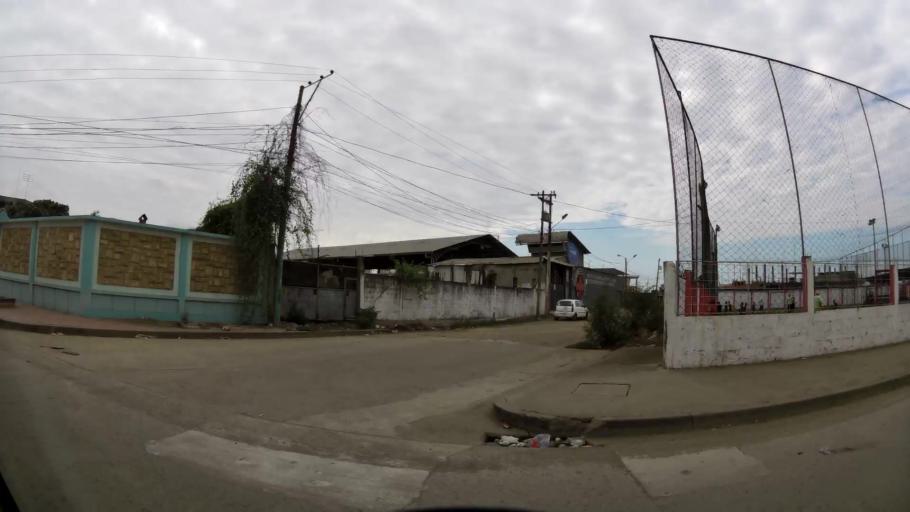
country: EC
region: El Oro
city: Machala
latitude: -3.2481
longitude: -79.9560
